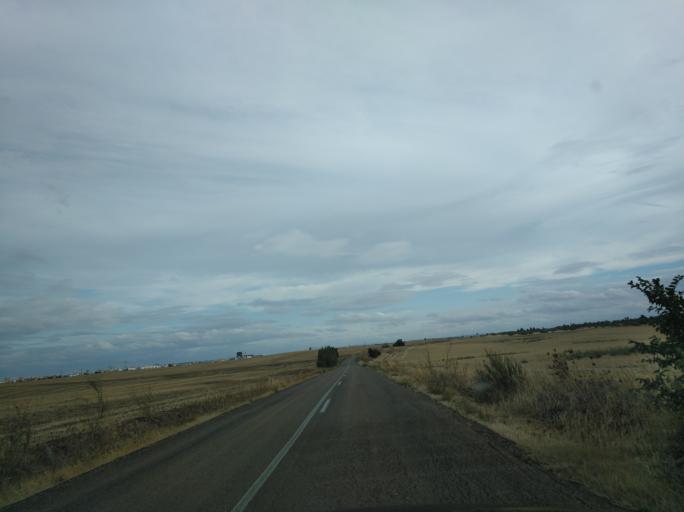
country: ES
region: Extremadura
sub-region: Provincia de Badajoz
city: Badajoz
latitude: 38.9030
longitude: -7.0180
